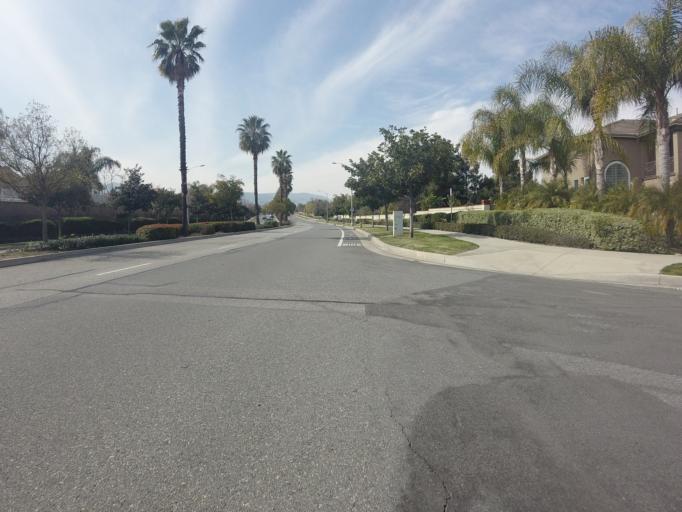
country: US
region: California
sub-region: Riverside County
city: El Cerrito
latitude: 33.8380
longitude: -117.5595
